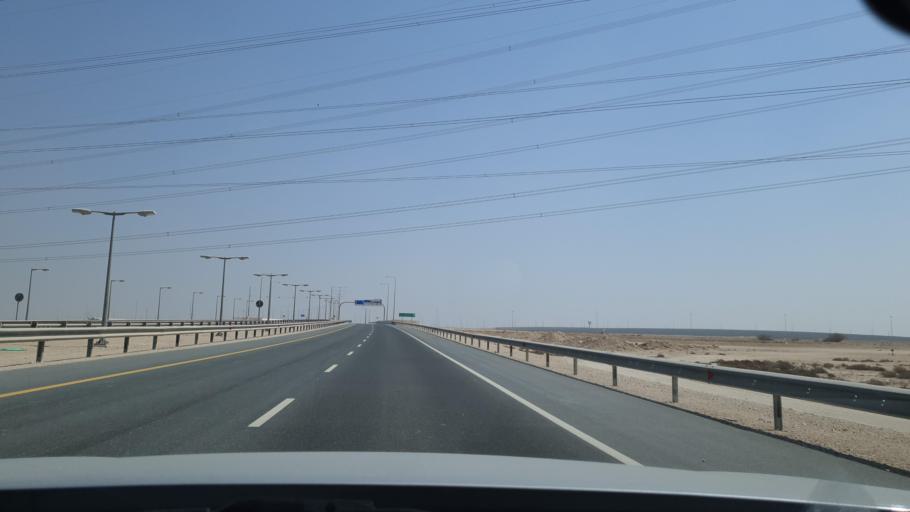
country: QA
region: Baladiyat az Za`ayin
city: Az Za`ayin
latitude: 25.6184
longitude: 51.3559
